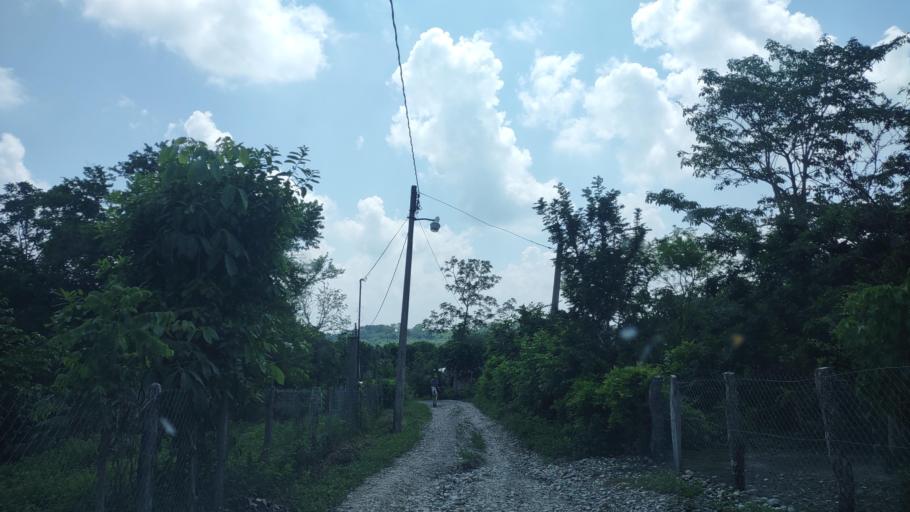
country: MX
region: Veracruz
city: Tempoal de Sanchez
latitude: 21.5471
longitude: -98.2741
